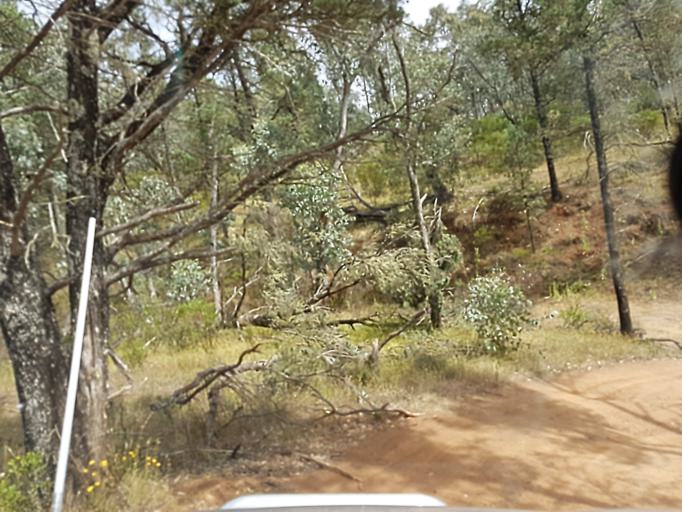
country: AU
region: New South Wales
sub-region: Snowy River
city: Jindabyne
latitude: -36.9299
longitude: 148.3977
